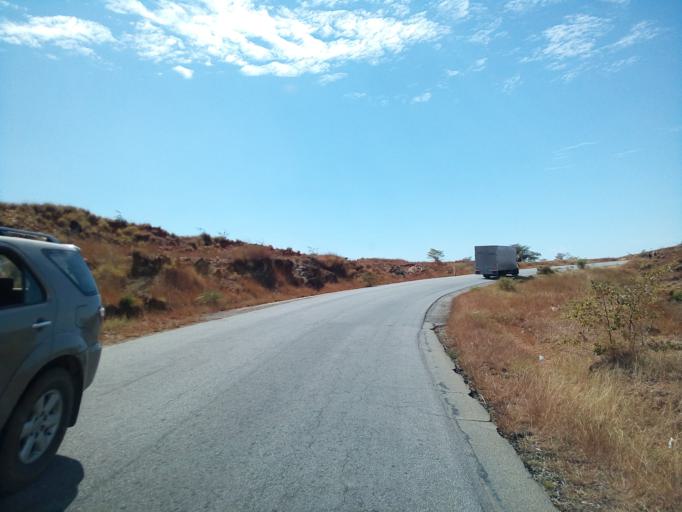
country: MG
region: Betsiboka
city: Maevatanana
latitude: -16.9449
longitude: 46.8550
